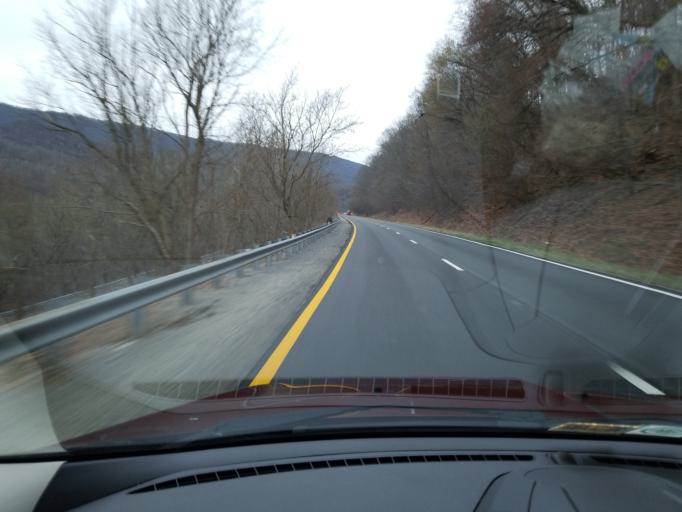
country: US
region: Virginia
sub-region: Giles County
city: Narrows
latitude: 37.3811
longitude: -80.8468
